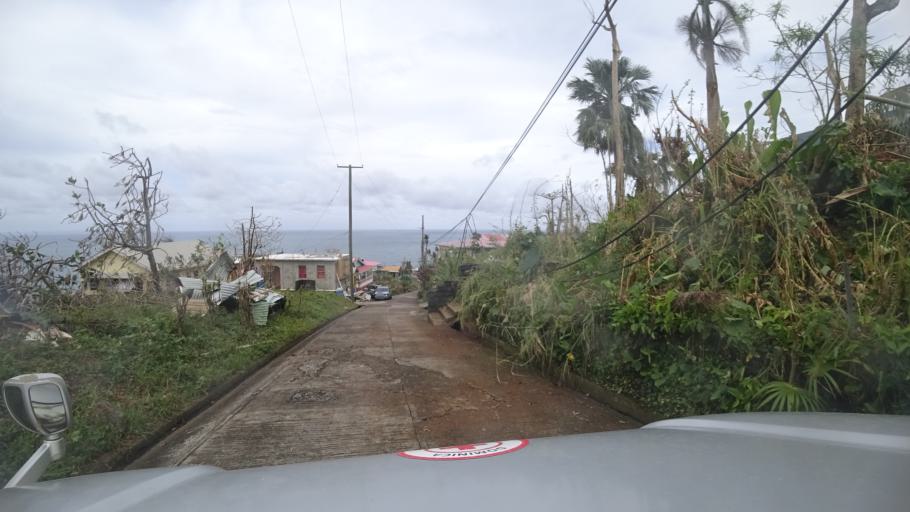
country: DM
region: Saint Andrew
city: Calibishie
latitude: 15.6146
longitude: -61.4073
